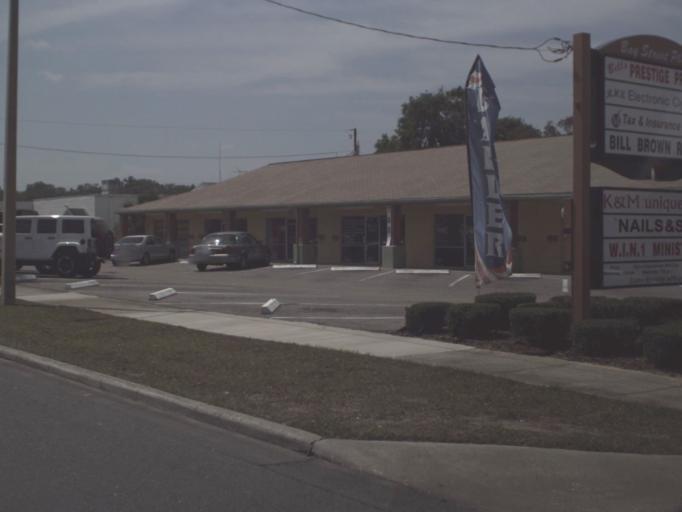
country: US
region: Florida
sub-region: Lake County
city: Eustis
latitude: 28.8471
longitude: -81.6856
